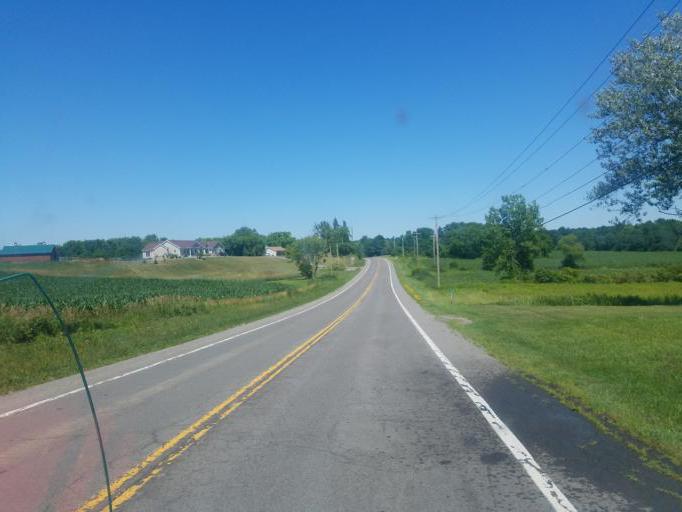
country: US
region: New York
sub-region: Ontario County
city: Geneva
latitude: 42.8441
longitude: -77.0266
